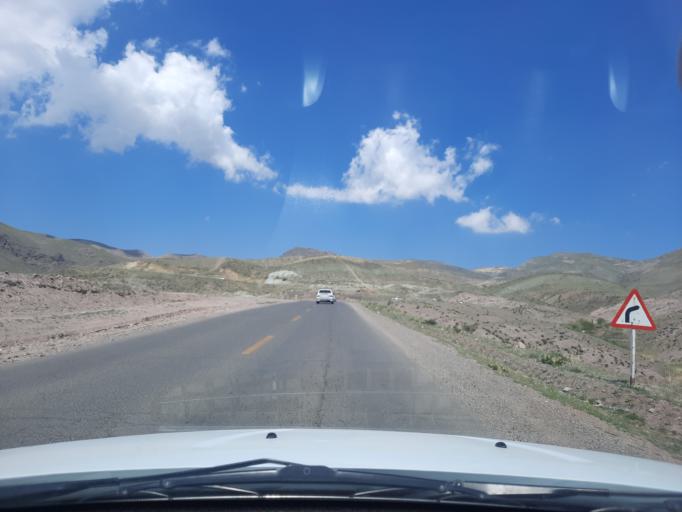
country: IR
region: Qazvin
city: Qazvin
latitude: 36.3503
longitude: 50.1870
